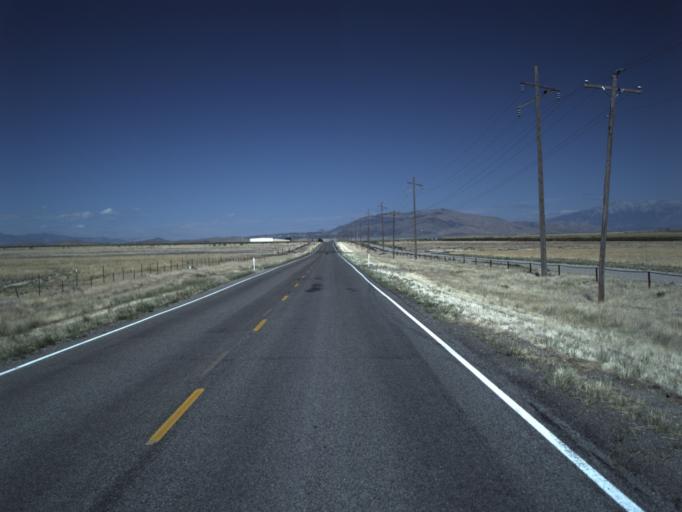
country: US
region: Utah
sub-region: Utah County
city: Genola
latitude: 39.9927
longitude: -111.9575
